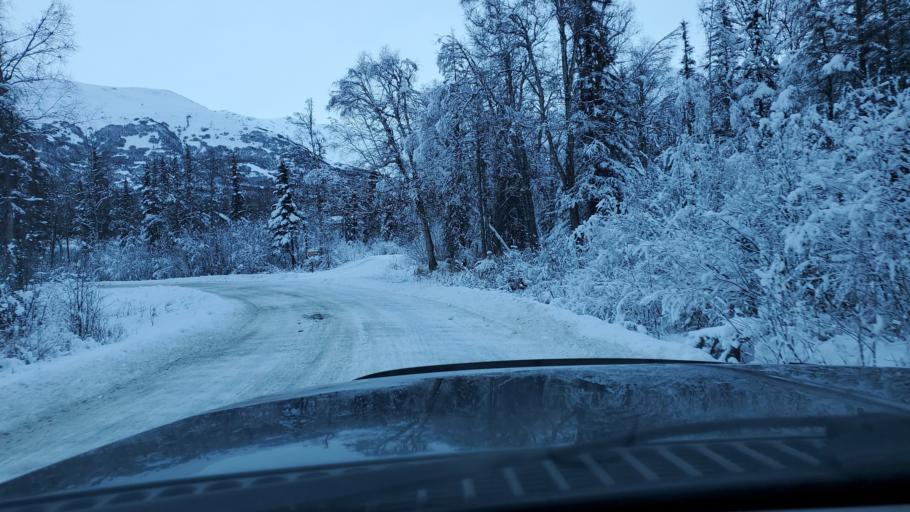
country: US
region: Alaska
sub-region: Matanuska-Susitna Borough
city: Lakes
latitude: 61.6962
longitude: -149.3225
